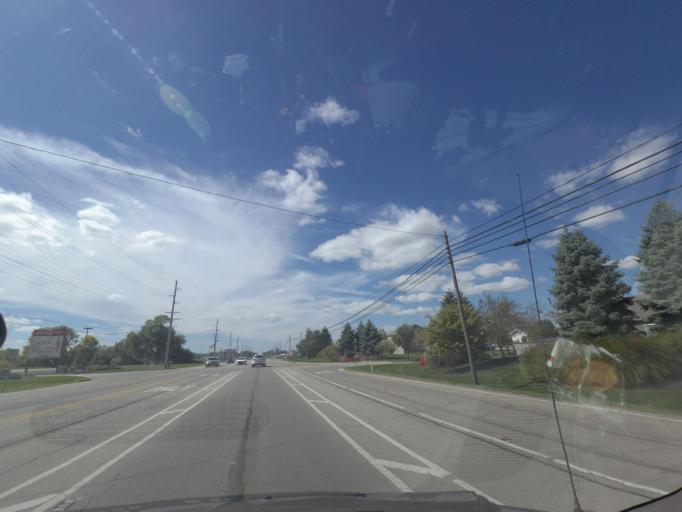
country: US
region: Indiana
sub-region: Hancock County
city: Greenfield
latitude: 39.7836
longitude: -85.8055
